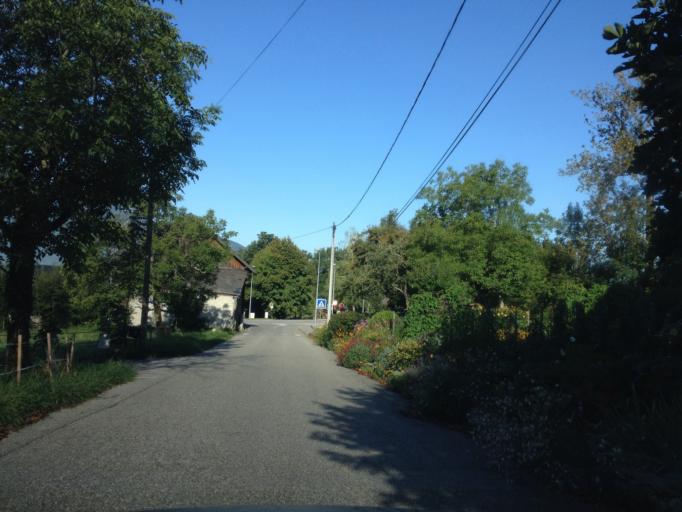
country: FR
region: Rhone-Alpes
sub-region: Departement de la Savoie
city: Mouxy
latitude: 45.6732
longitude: 5.9404
